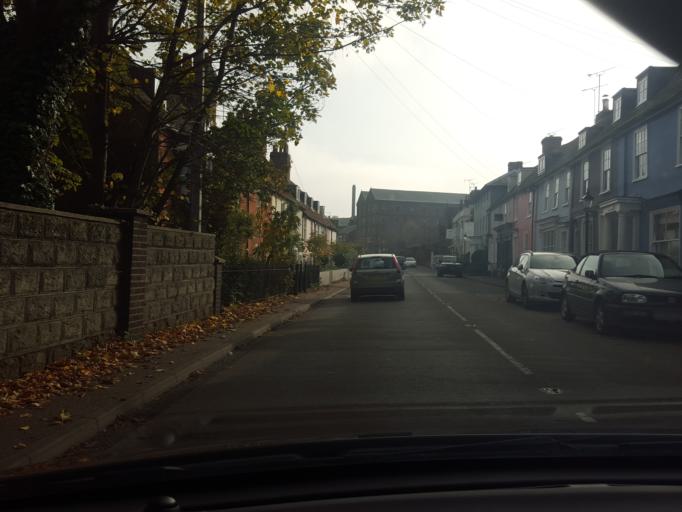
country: GB
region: England
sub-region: Essex
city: Mistley
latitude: 51.9454
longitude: 1.0784
